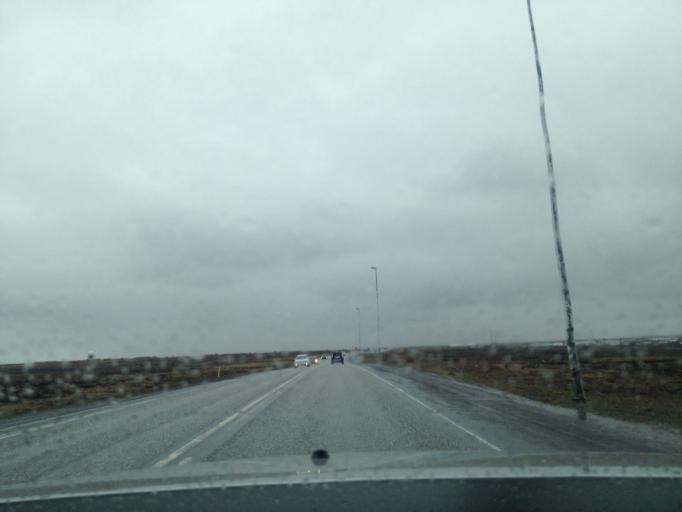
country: IS
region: Southern Peninsula
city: Reykjanesbaer
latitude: 63.9827
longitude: -22.5672
